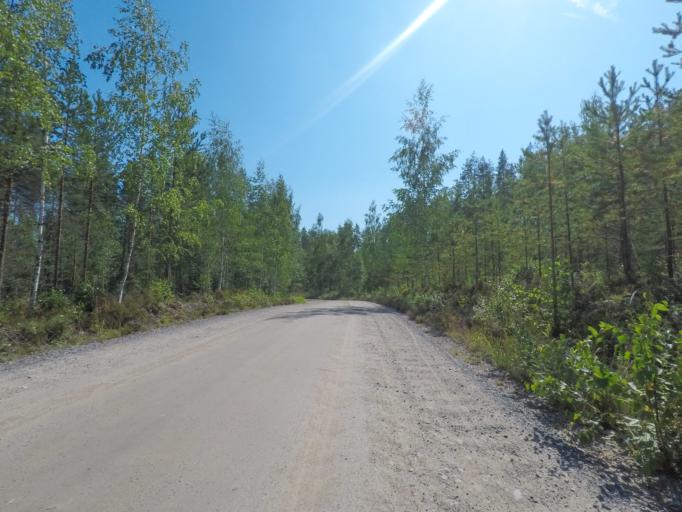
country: FI
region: Southern Savonia
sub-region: Mikkeli
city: Puumala
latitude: 61.4136
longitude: 28.0473
